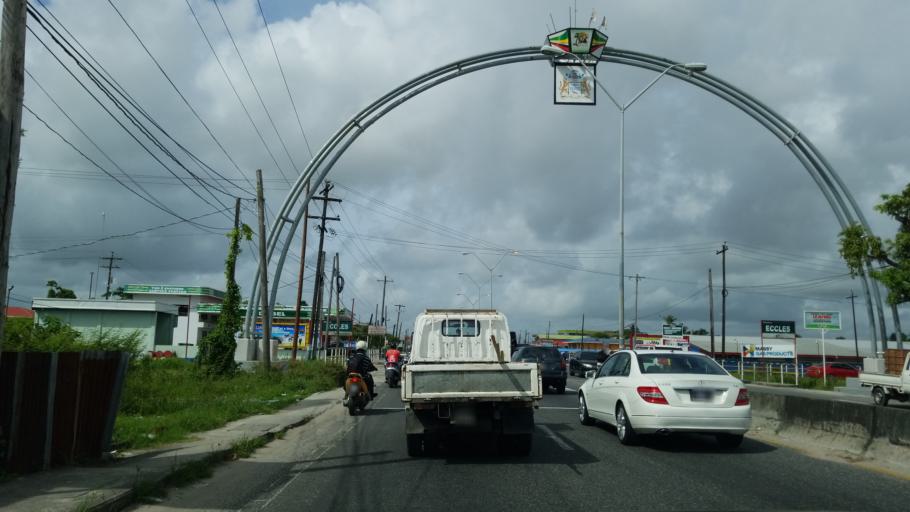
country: GY
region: Demerara-Mahaica
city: Georgetown
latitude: 6.7768
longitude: -58.1716
